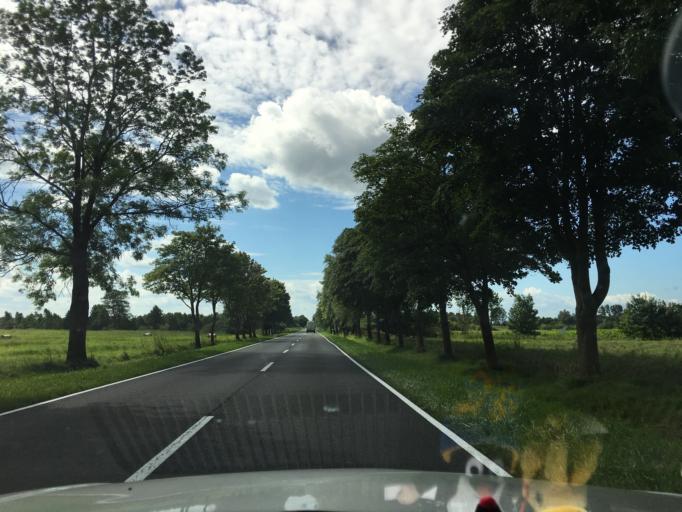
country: PL
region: West Pomeranian Voivodeship
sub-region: Powiat kamienski
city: Kamien Pomorski
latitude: 53.9299
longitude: 14.8109
